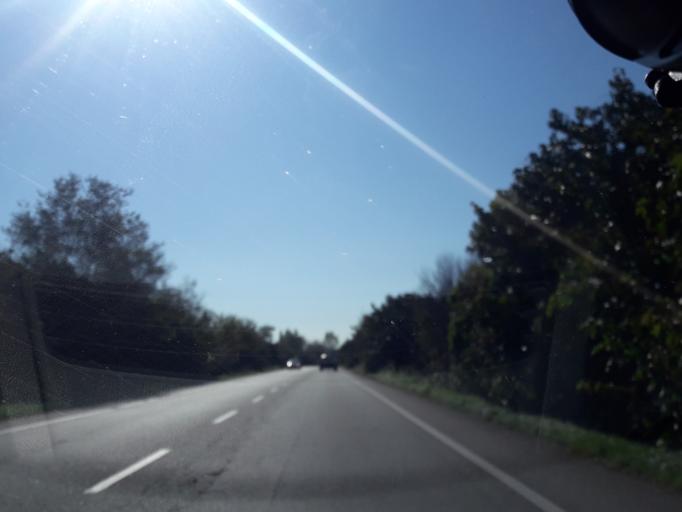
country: IT
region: Friuli Venezia Giulia
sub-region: Provincia di Udine
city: Povoletto
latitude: 46.1044
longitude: 13.2830
